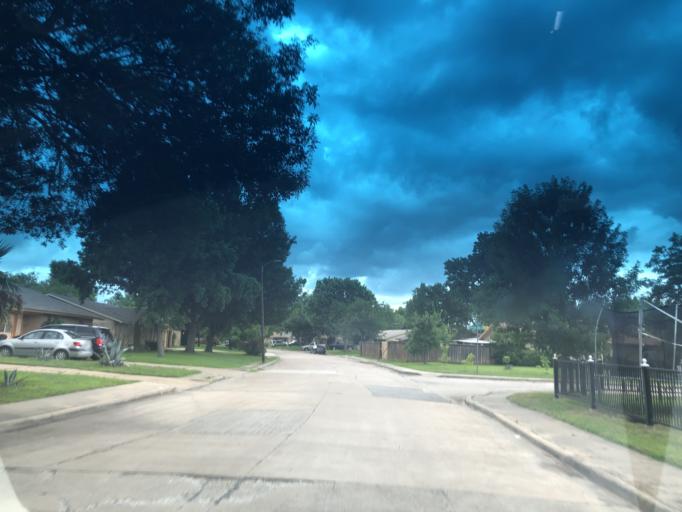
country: US
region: Texas
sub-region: Dallas County
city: Grand Prairie
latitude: 32.7054
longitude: -97.0052
